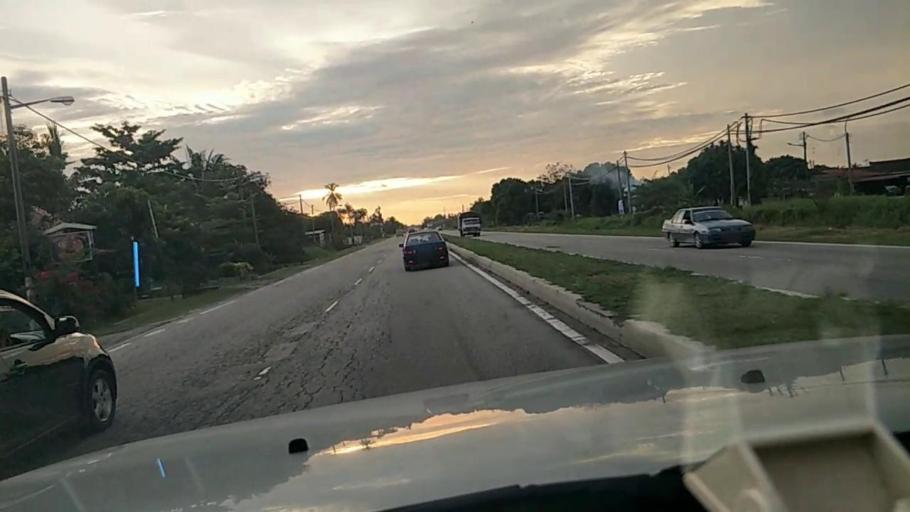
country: MY
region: Perak
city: Kampong Dungun
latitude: 3.1410
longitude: 101.3639
